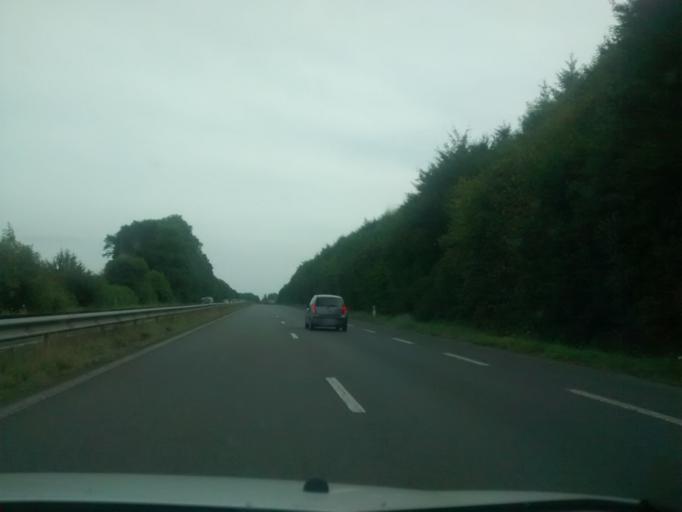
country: FR
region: Brittany
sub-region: Departement d'Ille-et-Vilaine
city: Pleugueneuc
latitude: 48.4160
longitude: -1.9091
